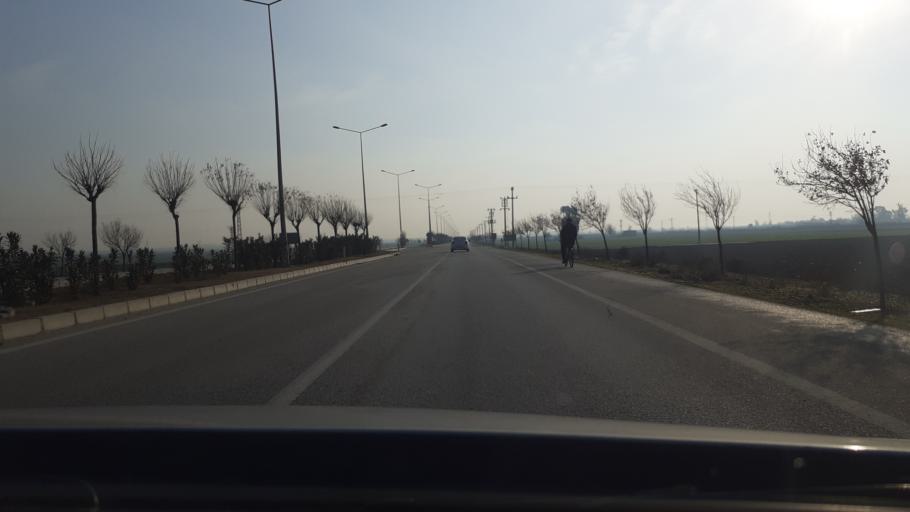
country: TR
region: Hatay
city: Serinyol
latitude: 36.3719
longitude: 36.2316
